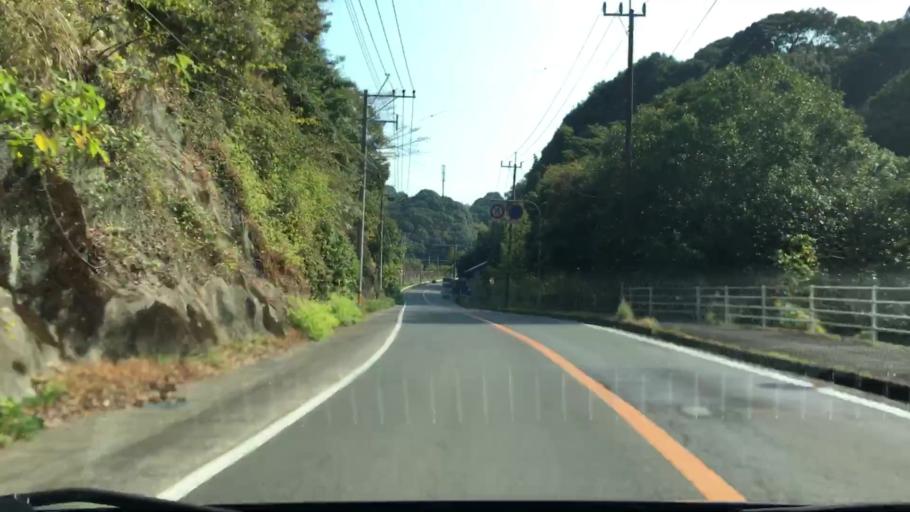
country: JP
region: Nagasaki
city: Togitsu
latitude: 32.9567
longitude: 129.7832
